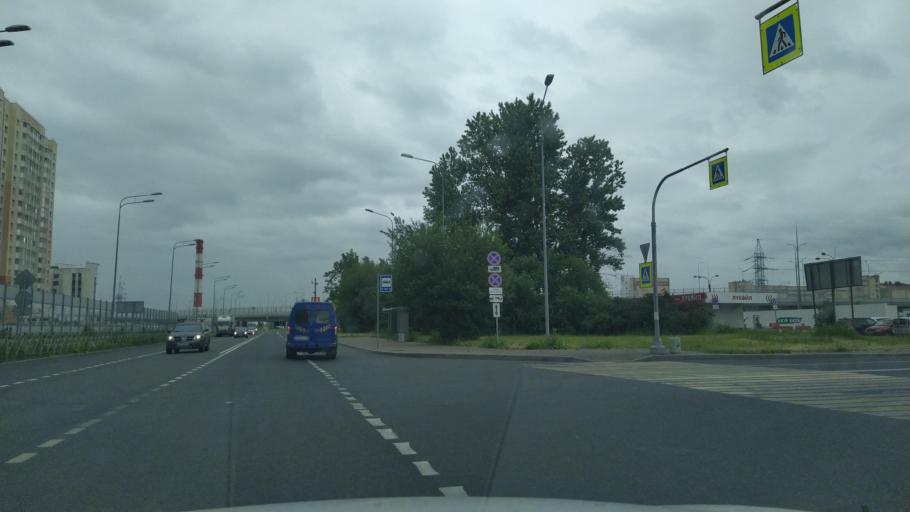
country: RU
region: St.-Petersburg
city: Kupchino
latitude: 59.8348
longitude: 30.3112
